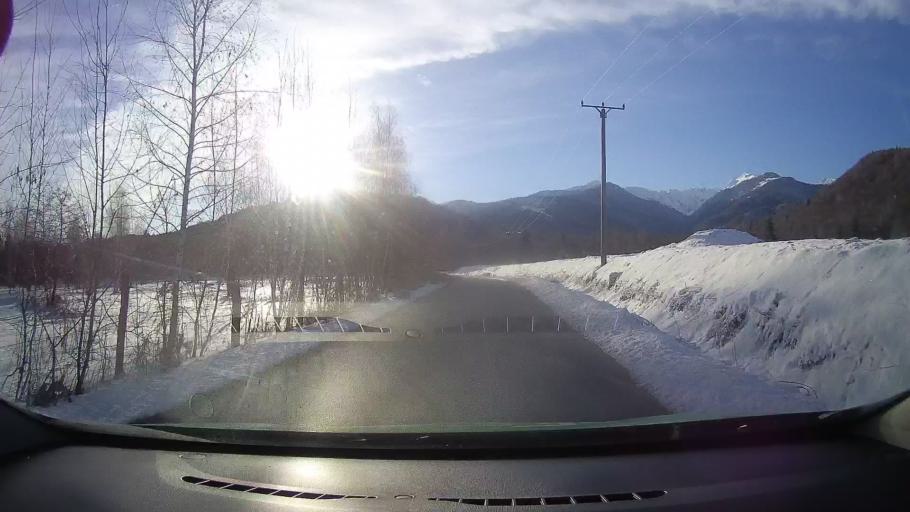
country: RO
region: Sibiu
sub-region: Comuna Cartisoara
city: Cartisoara
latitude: 45.6958
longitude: 24.6096
